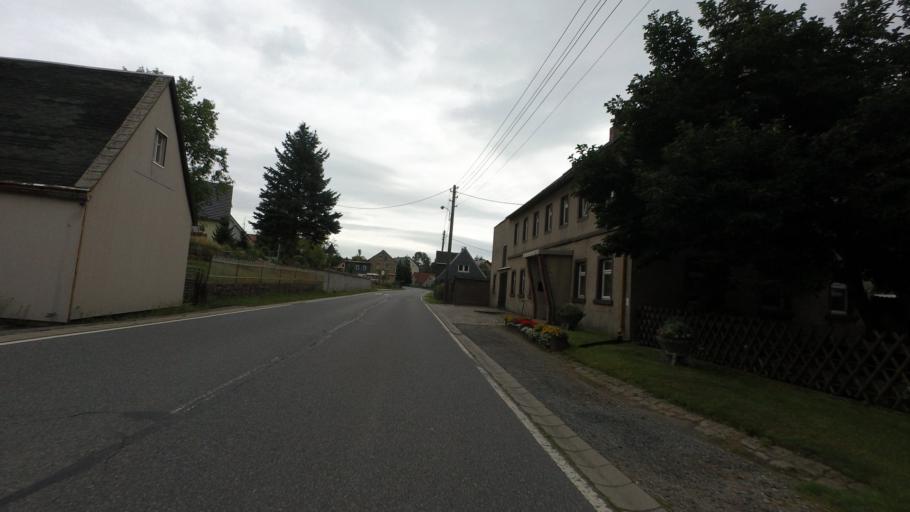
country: DE
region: Saxony
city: Berthelsdorf
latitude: 51.0496
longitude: 14.2232
